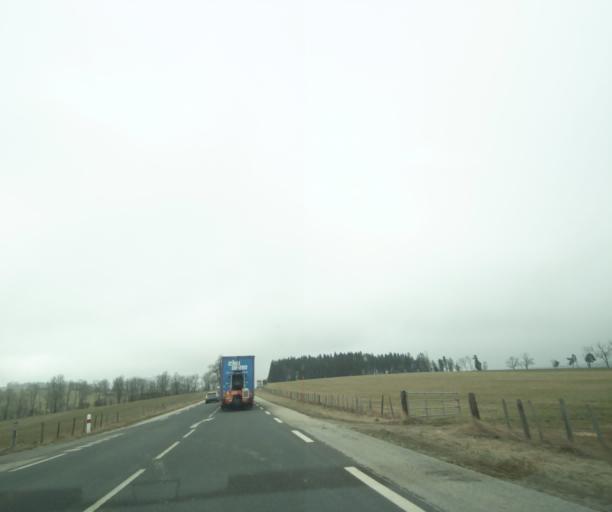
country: FR
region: Languedoc-Roussillon
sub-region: Departement de la Lozere
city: Langogne
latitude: 44.7036
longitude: 3.8193
